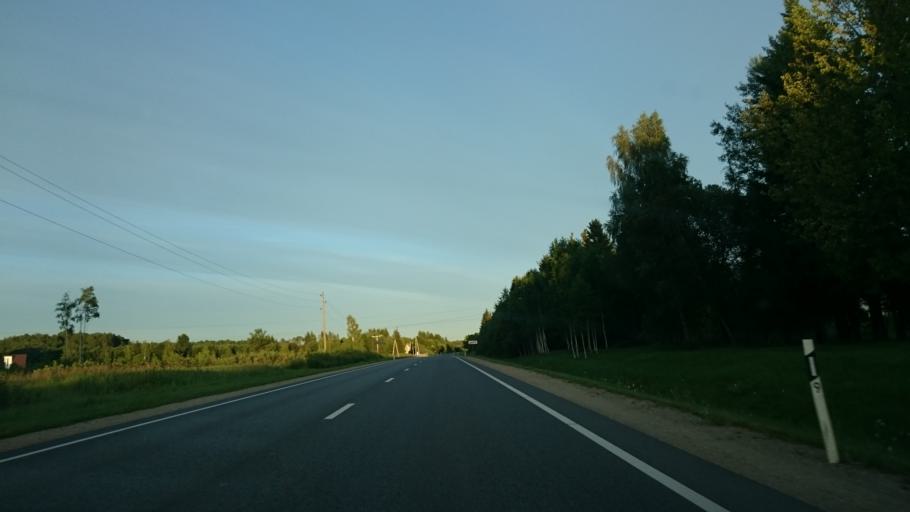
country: LV
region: Broceni
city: Broceni
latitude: 56.6787
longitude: 22.5760
